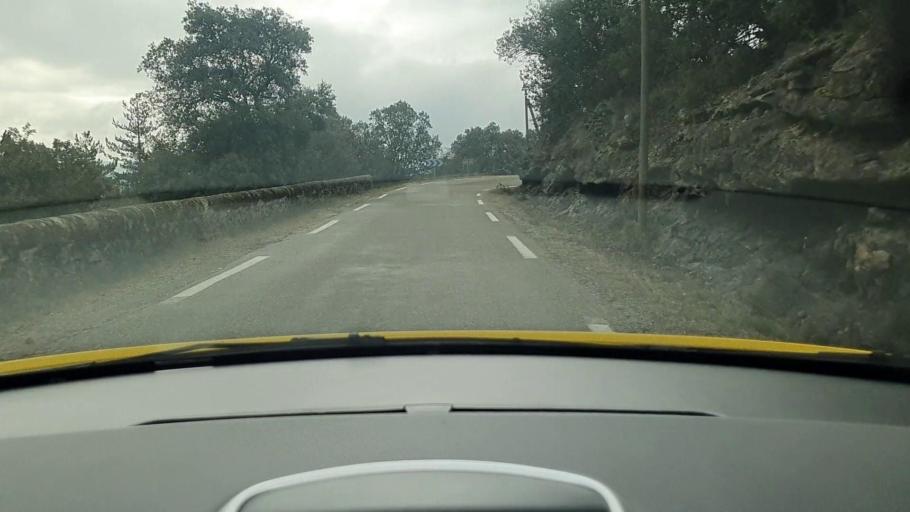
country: FR
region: Languedoc-Roussillon
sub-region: Departement du Gard
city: Besseges
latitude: 44.3457
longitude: 4.0316
